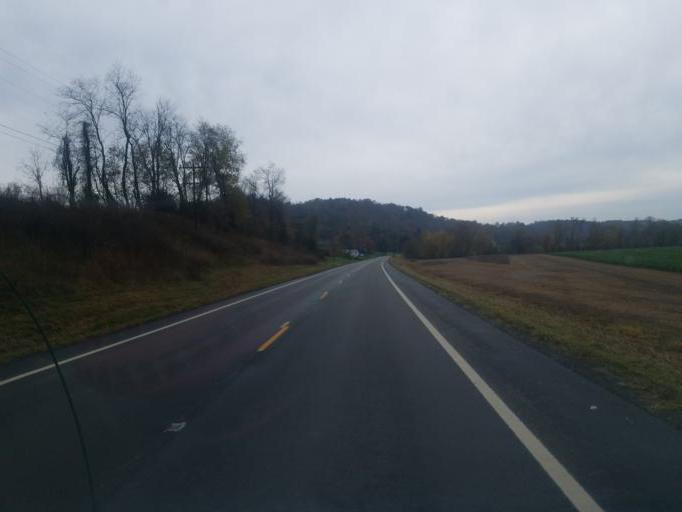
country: US
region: Ohio
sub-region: Washington County
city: Beverly
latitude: 39.5560
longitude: -81.5576
